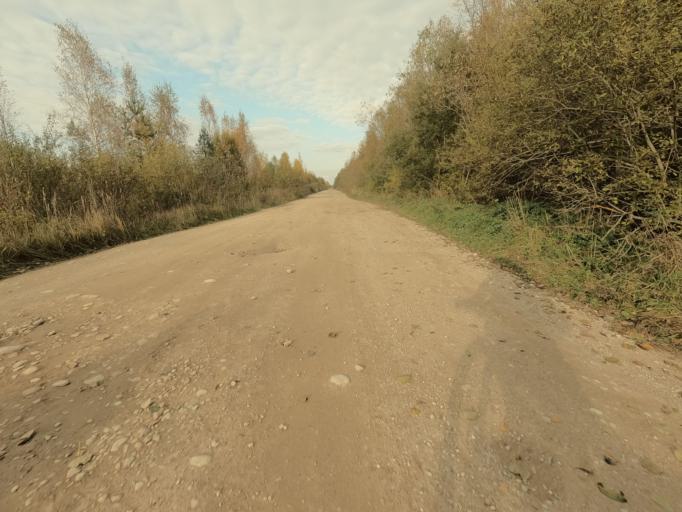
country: RU
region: Novgorod
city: Volkhovskiy
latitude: 58.9078
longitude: 31.0378
